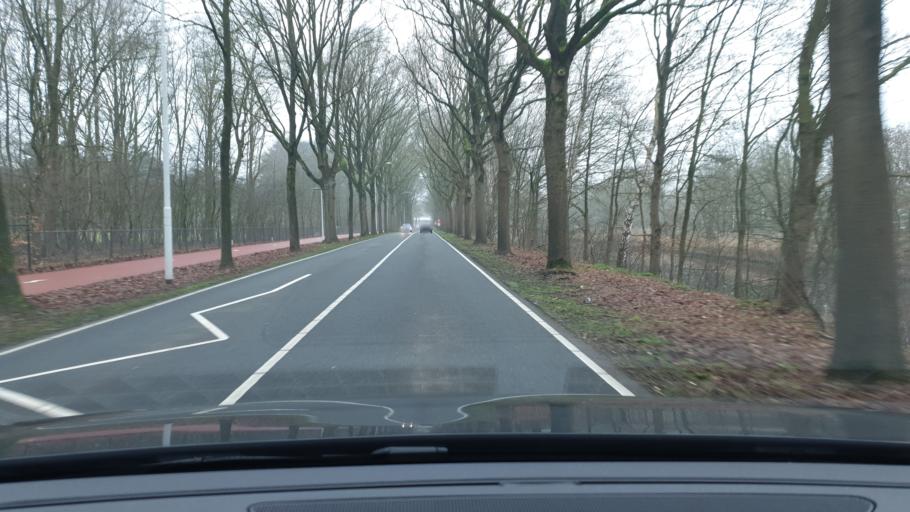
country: NL
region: North Brabant
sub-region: Gemeente Best
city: Best
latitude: 51.4974
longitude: 5.4085
